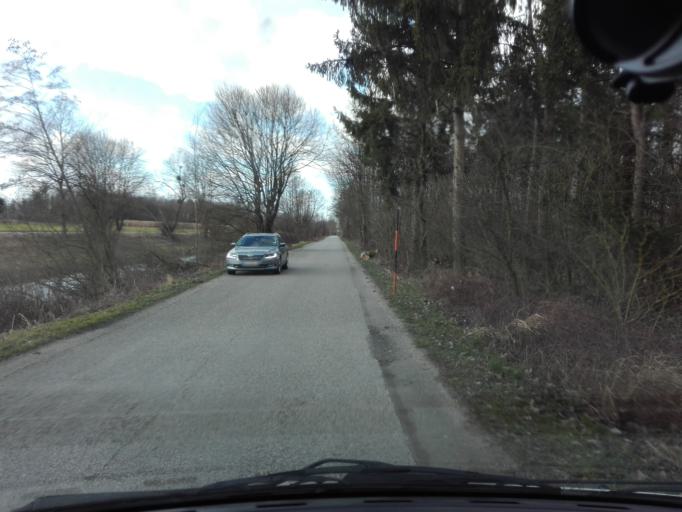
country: AT
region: Upper Austria
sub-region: Politischer Bezirk Perg
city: Perg
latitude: 48.2265
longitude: 14.6564
